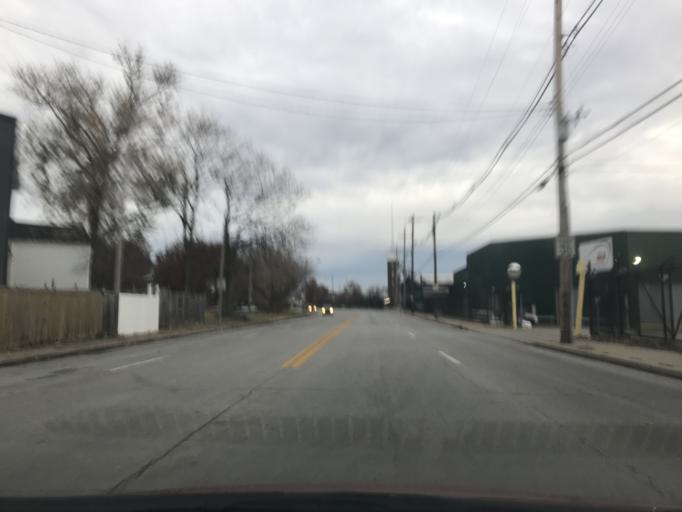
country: US
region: Kentucky
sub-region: Jefferson County
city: Louisville
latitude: 38.2477
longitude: -85.7346
